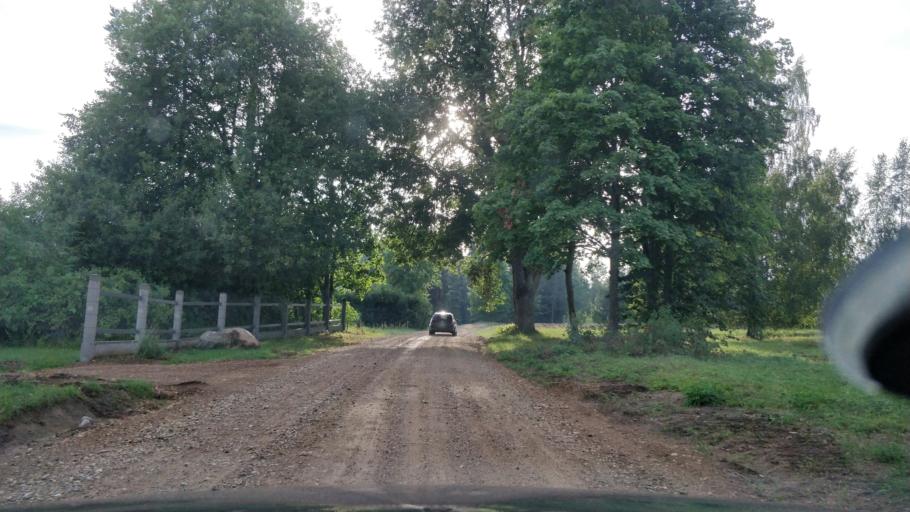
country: LV
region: Sigulda
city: Sigulda
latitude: 57.1005
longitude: 24.8165
